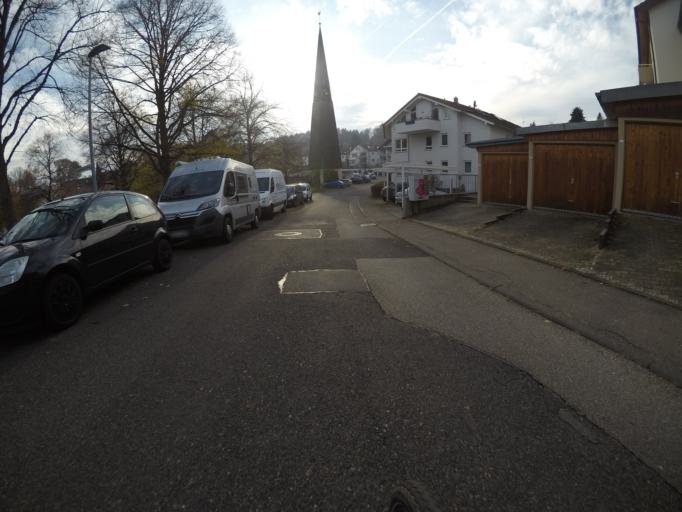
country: DE
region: Baden-Wuerttemberg
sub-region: Regierungsbezirk Stuttgart
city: Steinenbronn
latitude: 48.7048
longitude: 9.1186
